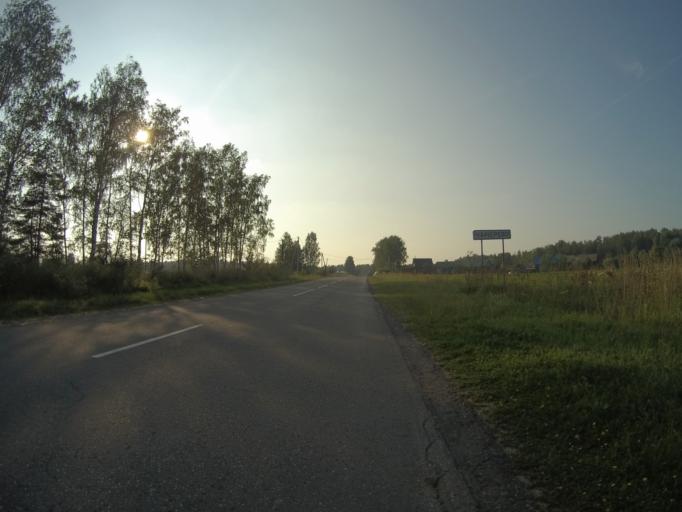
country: RU
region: Vladimir
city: Sudogda
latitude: 56.0671
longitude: 40.8015
